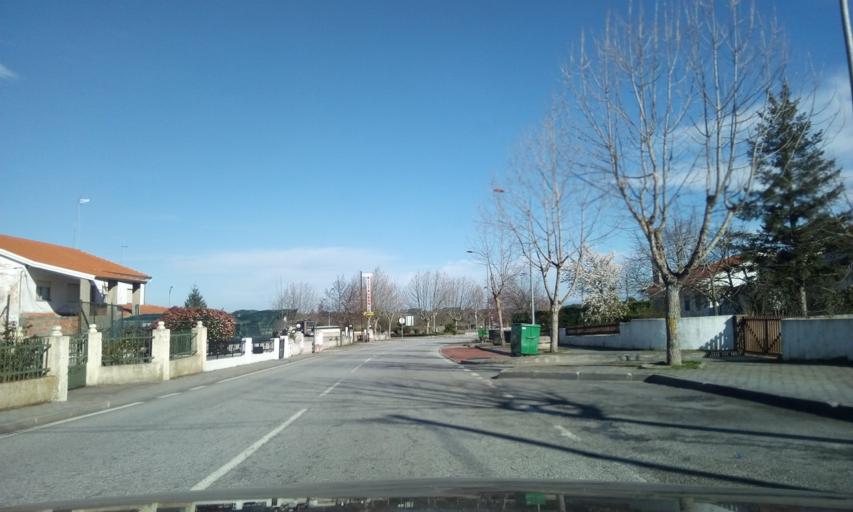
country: ES
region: Castille and Leon
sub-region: Provincia de Salamanca
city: Fuentes de Onoro
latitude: 40.6176
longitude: -6.8437
